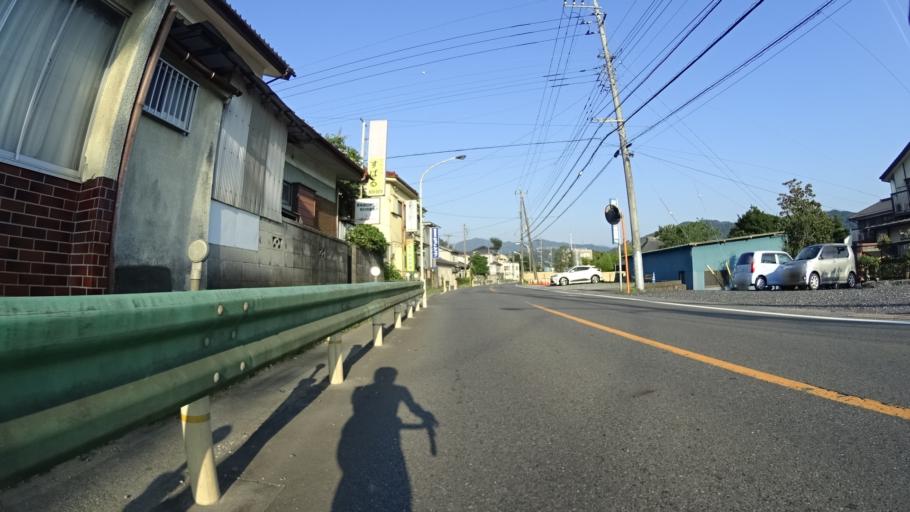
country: JP
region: Tokyo
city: Ome
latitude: 35.7826
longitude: 139.2535
